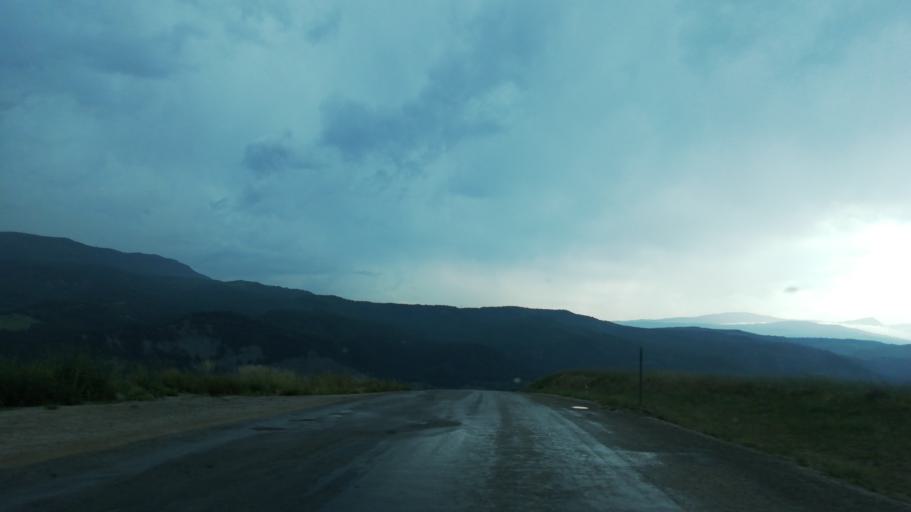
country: TR
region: Karabuk
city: Safranbolu
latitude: 41.2259
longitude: 32.6869
